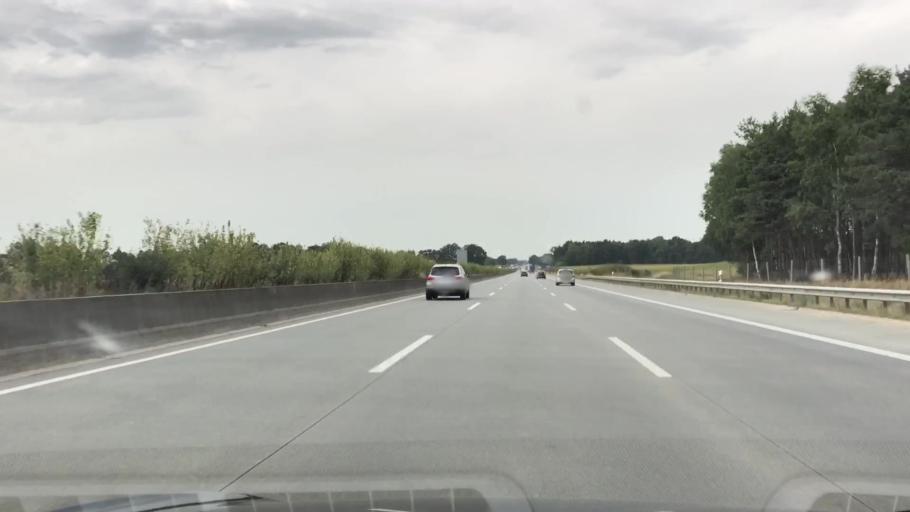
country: DE
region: Lower Saxony
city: Gross Meckelsen
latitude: 53.2638
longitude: 9.4430
